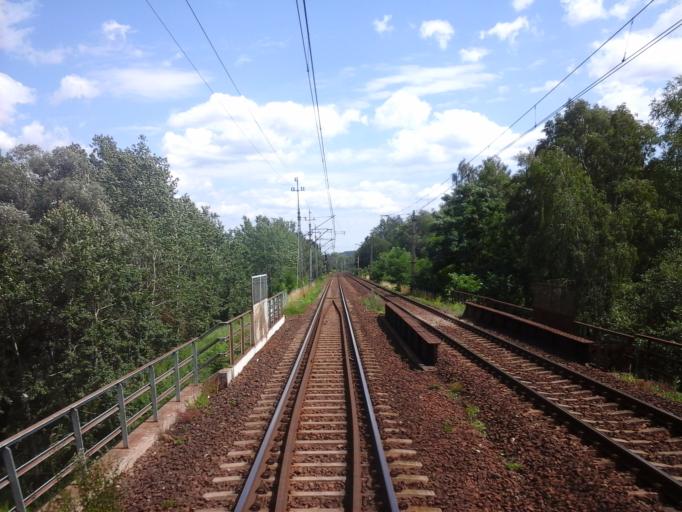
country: PL
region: West Pomeranian Voivodeship
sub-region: Szczecin
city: Szczecin
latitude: 53.3755
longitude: 14.5865
